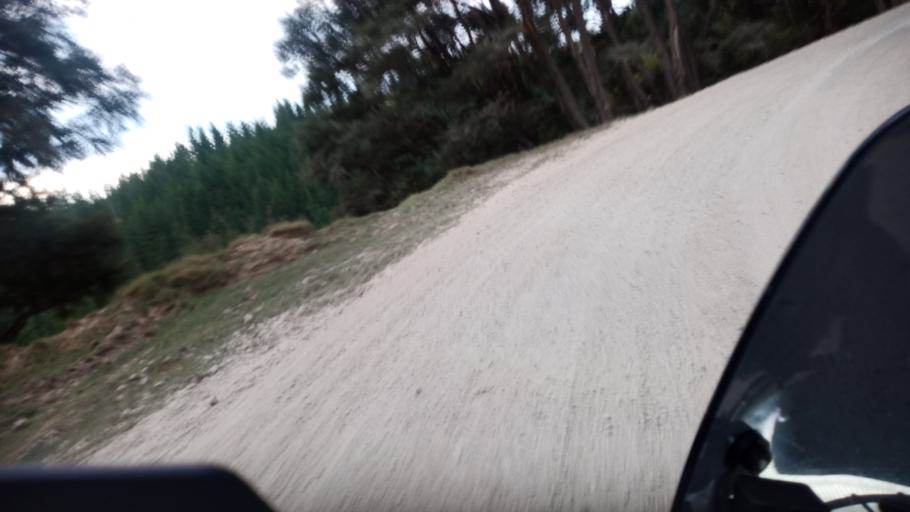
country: NZ
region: Gisborne
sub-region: Gisborne District
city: Gisborne
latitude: -38.4790
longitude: 177.9727
